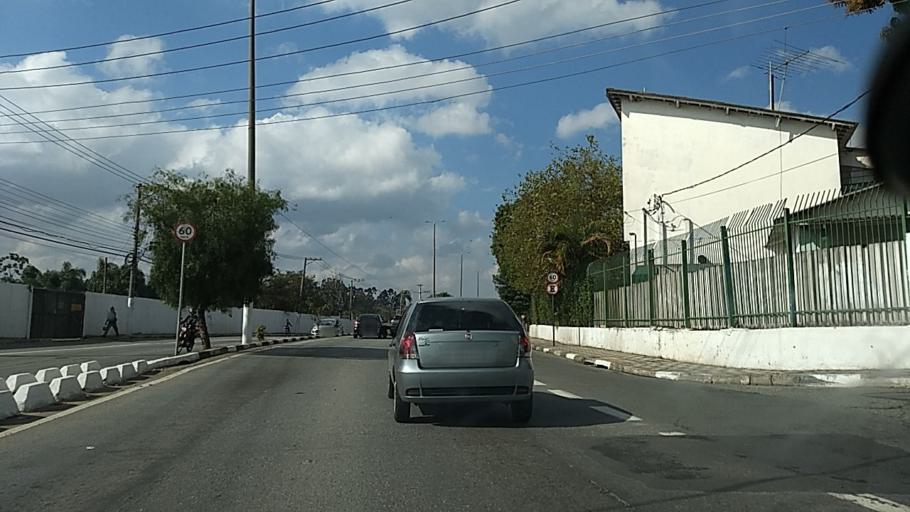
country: BR
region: Sao Paulo
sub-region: Osasco
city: Osasco
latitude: -23.5237
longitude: -46.8100
